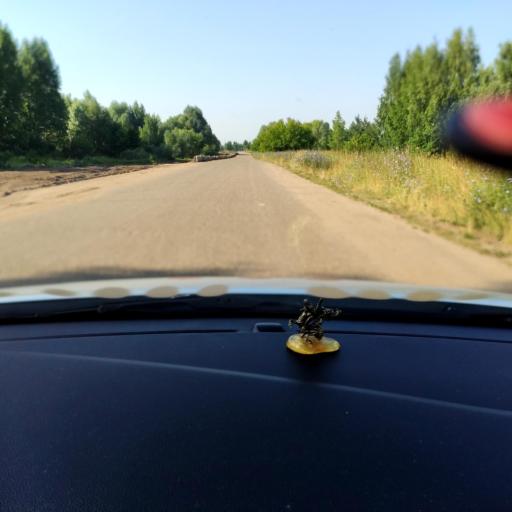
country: RU
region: Tatarstan
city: Stolbishchi
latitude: 55.6987
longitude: 49.2233
